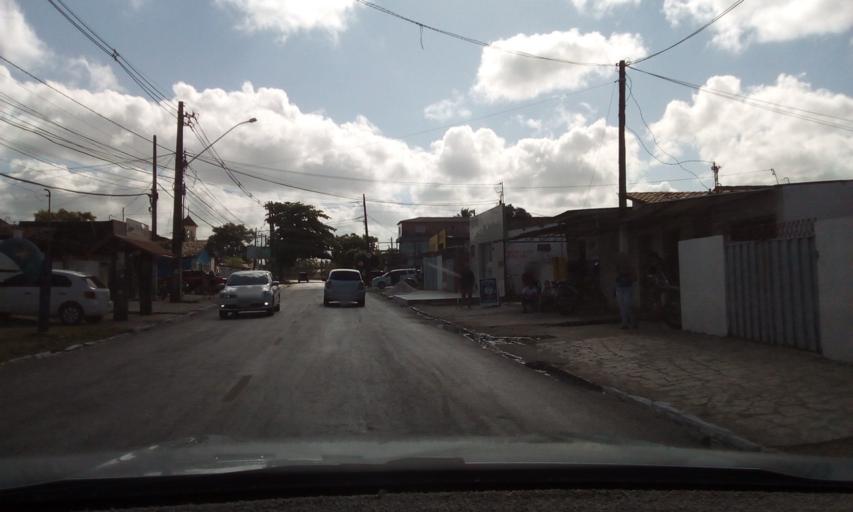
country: BR
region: Paraiba
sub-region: Bayeux
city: Bayeux
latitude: -7.1571
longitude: -34.9049
